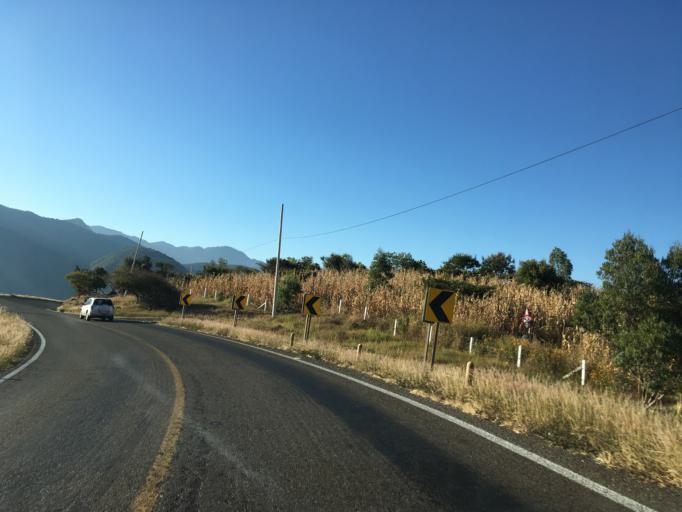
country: MX
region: Michoacan
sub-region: Tuxpan
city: La Soledad
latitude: 19.5139
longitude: -100.4700
